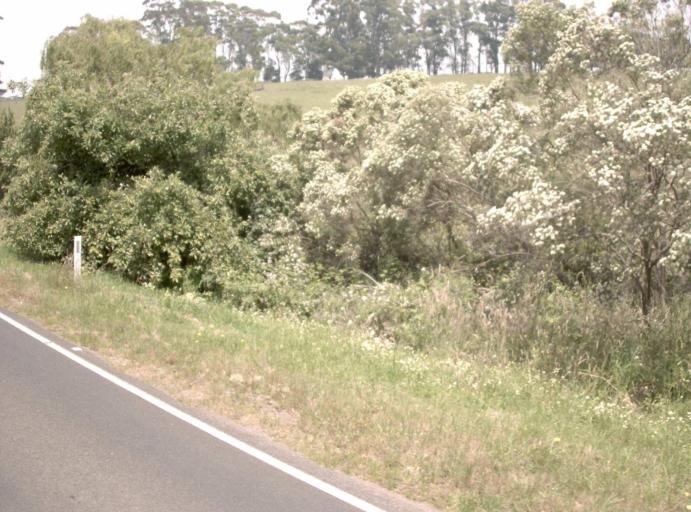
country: AU
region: Victoria
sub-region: Latrobe
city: Traralgon
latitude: -38.3586
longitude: 146.7222
